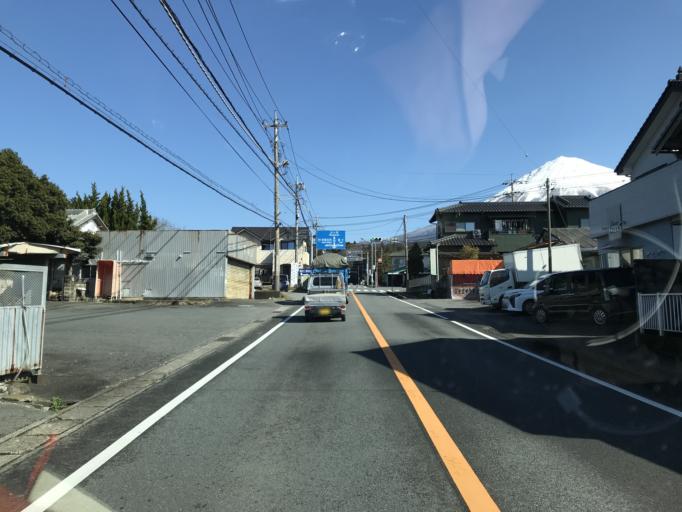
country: JP
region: Shizuoka
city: Fujinomiya
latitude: 35.2624
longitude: 138.6331
